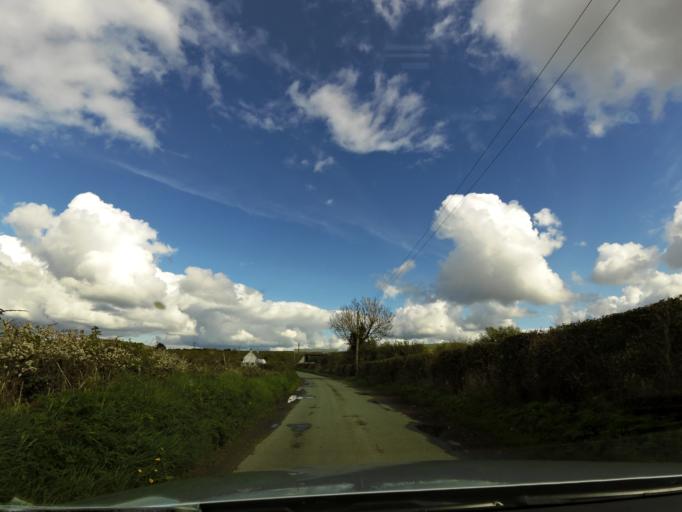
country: IE
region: Leinster
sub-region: Laois
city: Rathdowney
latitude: 52.7782
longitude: -7.5405
